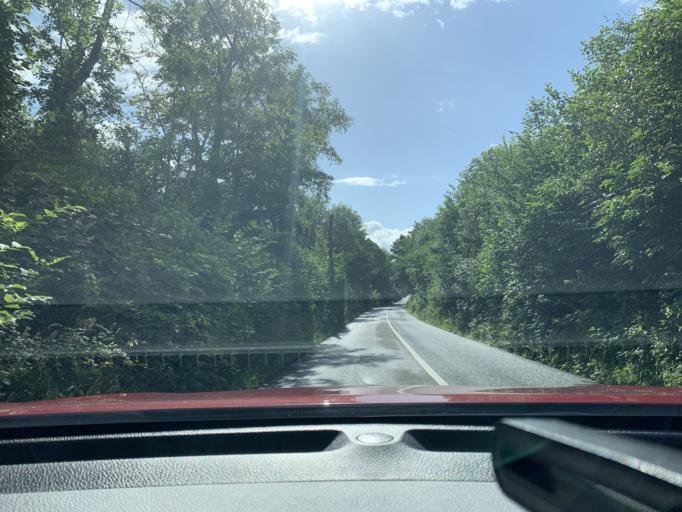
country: IE
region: Connaught
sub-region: Sligo
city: Strandhill
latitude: 54.3556
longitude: -8.5722
